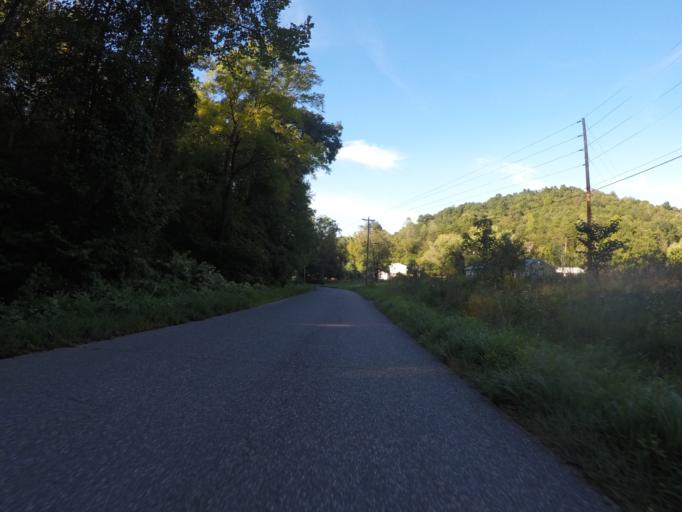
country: US
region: Ohio
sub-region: Lawrence County
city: Coal Grove
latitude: 38.5345
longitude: -82.5323
